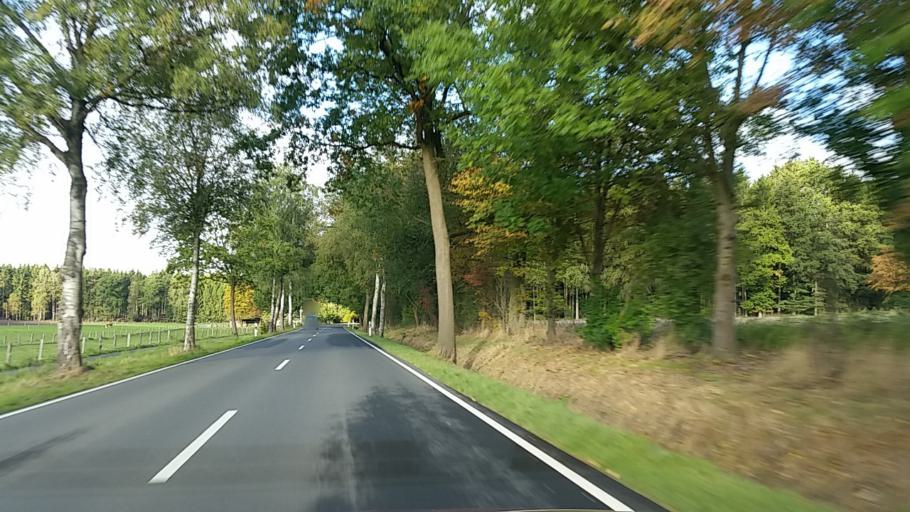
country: DE
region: Lower Saxony
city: Bad Fallingbostel
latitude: 52.9083
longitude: 9.7296
